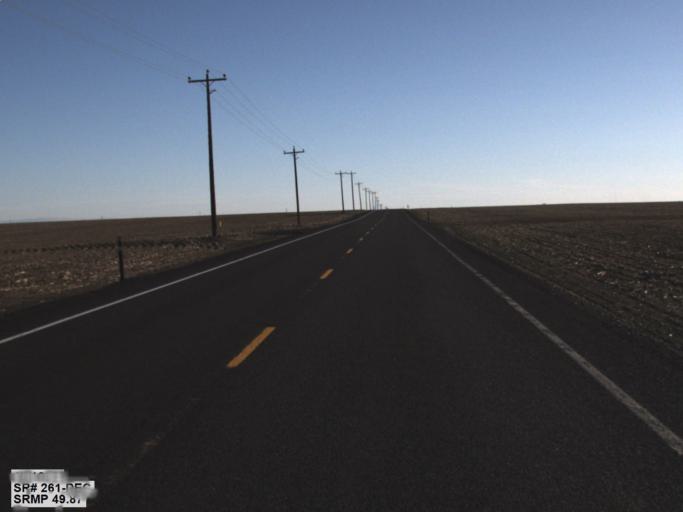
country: US
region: Washington
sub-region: Adams County
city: Ritzville
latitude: 46.9354
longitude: -118.3434
